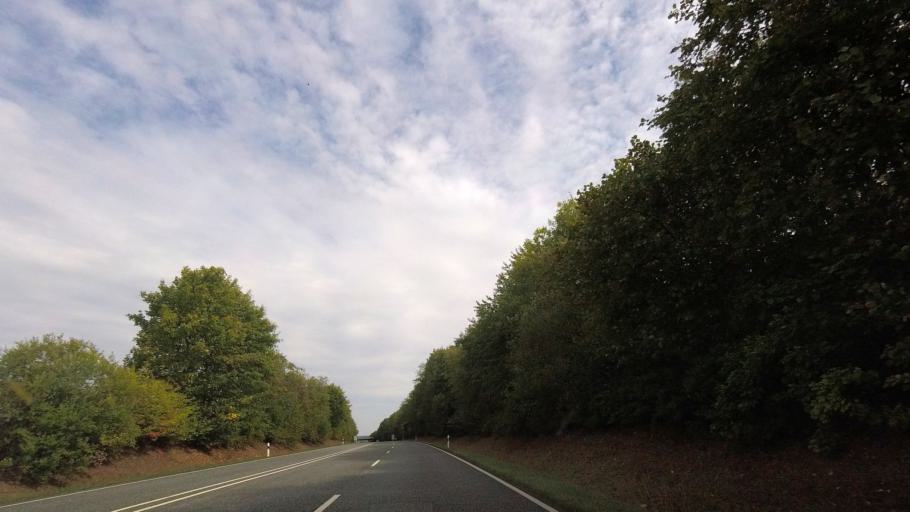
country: DE
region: Hesse
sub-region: Regierungsbezirk Kassel
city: Friedewald
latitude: 50.8799
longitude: 9.8614
